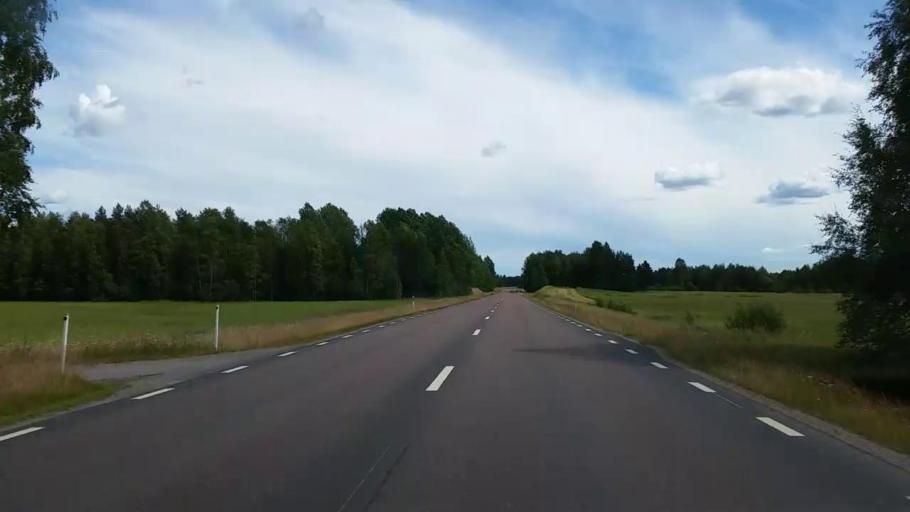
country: SE
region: Gaevleborg
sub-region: Ovanakers Kommun
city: Edsbyn
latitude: 61.3668
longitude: 15.8734
